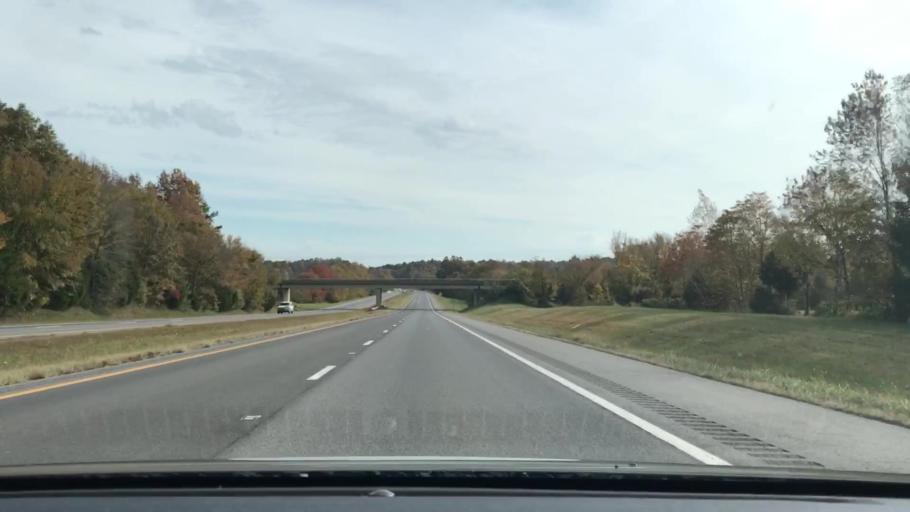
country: US
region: Kentucky
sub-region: Graves County
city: Mayfield
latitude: 36.7883
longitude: -88.5341
